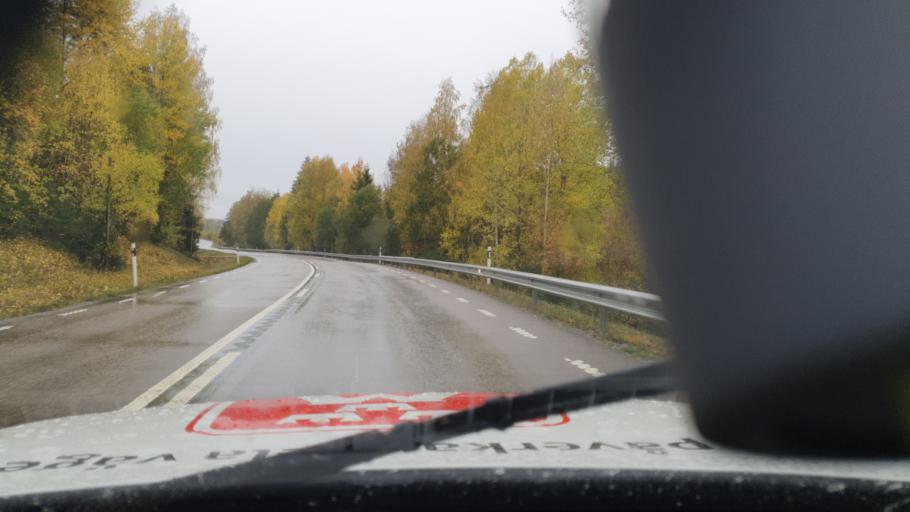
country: SE
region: Vaestra Goetaland
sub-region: Bengtsfors Kommun
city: Billingsfors
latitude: 58.9412
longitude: 12.1091
